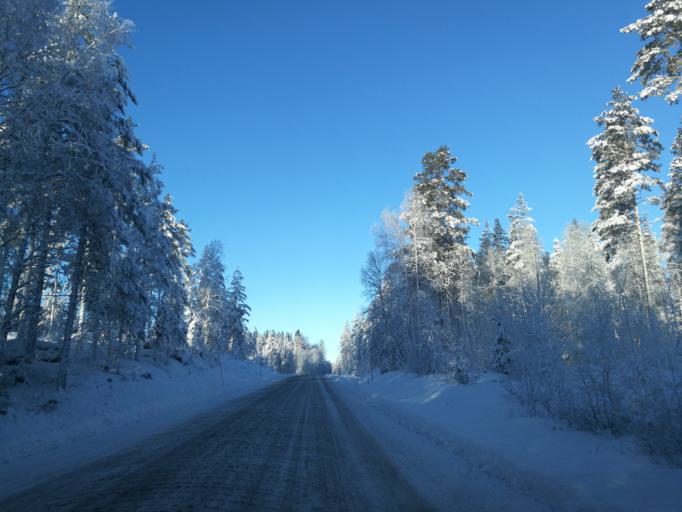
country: NO
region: Hedmark
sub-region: Grue
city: Kirkenaer
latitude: 60.5470
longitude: 12.5417
